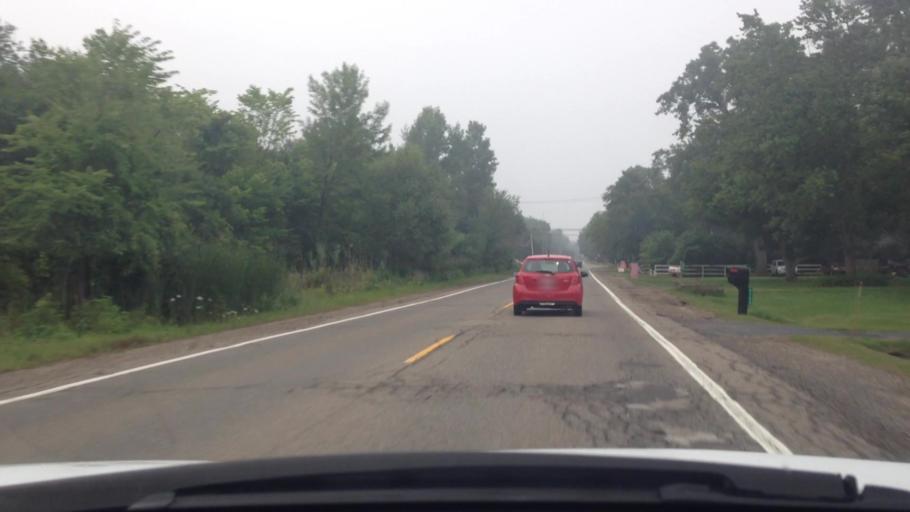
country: US
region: Michigan
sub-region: Oakland County
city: Waterford
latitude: 42.7149
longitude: -83.3491
